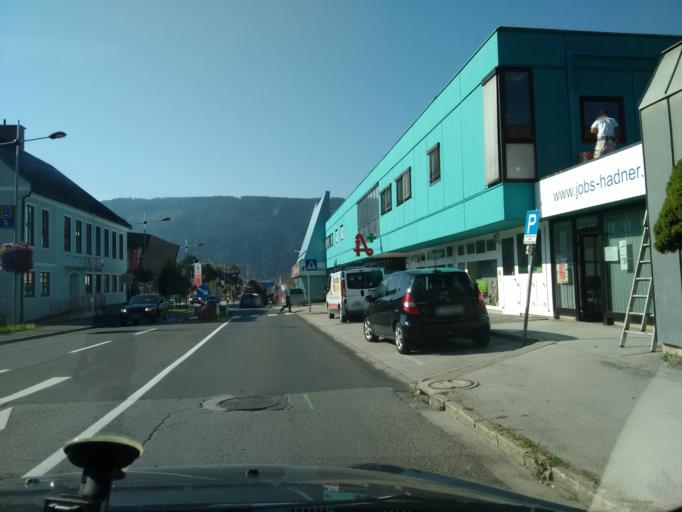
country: AT
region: Styria
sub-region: Politischer Bezirk Liezen
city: Liezen
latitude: 47.5651
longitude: 14.2439
